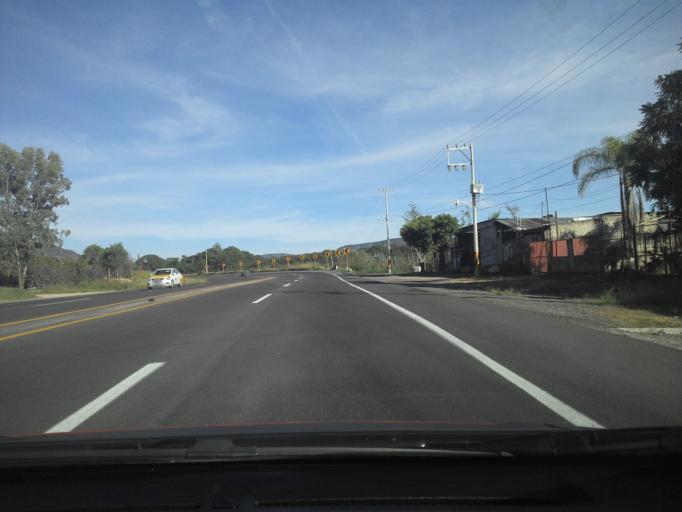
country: MX
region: Jalisco
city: La Venta del Astillero
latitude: 20.7279
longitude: -103.6175
